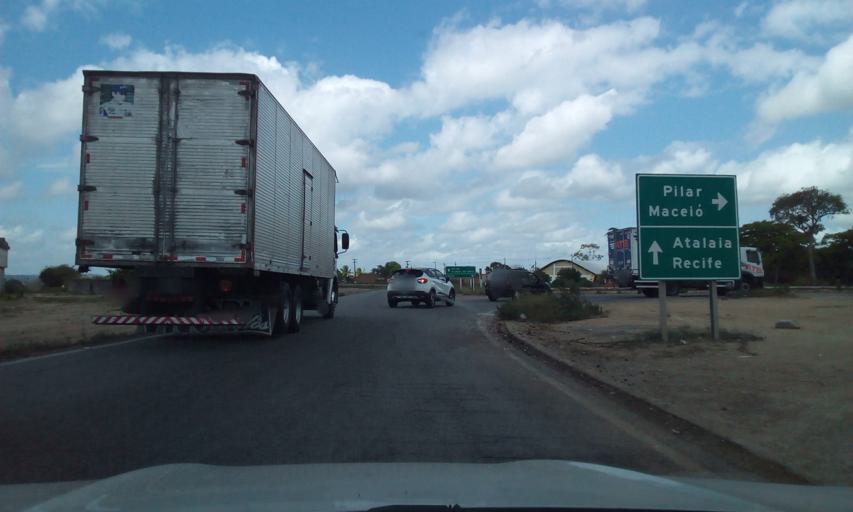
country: BR
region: Alagoas
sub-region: Pilar
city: Pilar
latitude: -9.5672
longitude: -35.9697
